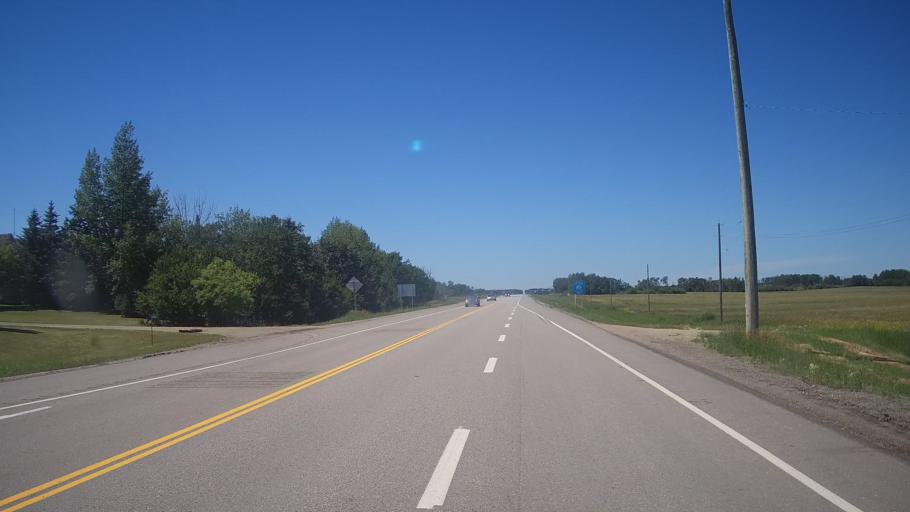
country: CA
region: Manitoba
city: Minnedosa
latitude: 50.2700
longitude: -99.9095
